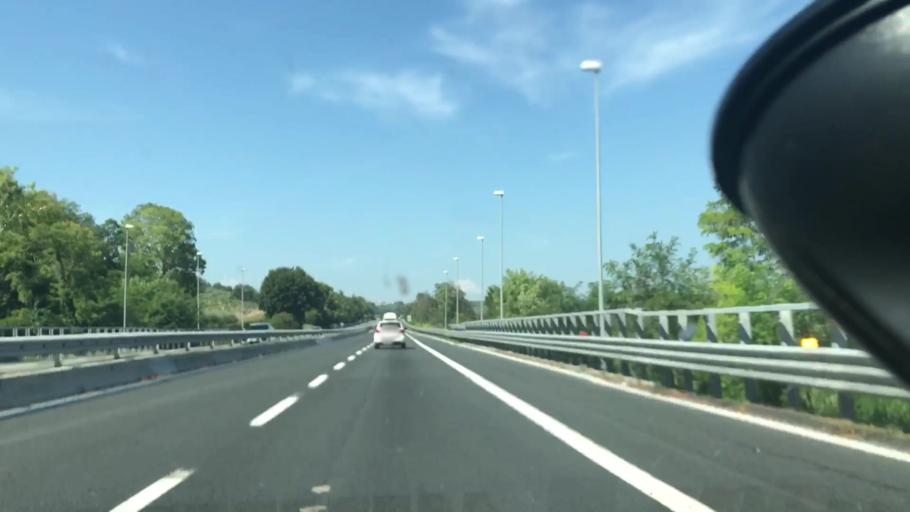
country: IT
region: Abruzzo
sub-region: Provincia di Chieti
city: Torino di Sangro
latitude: 42.2011
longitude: 14.5606
